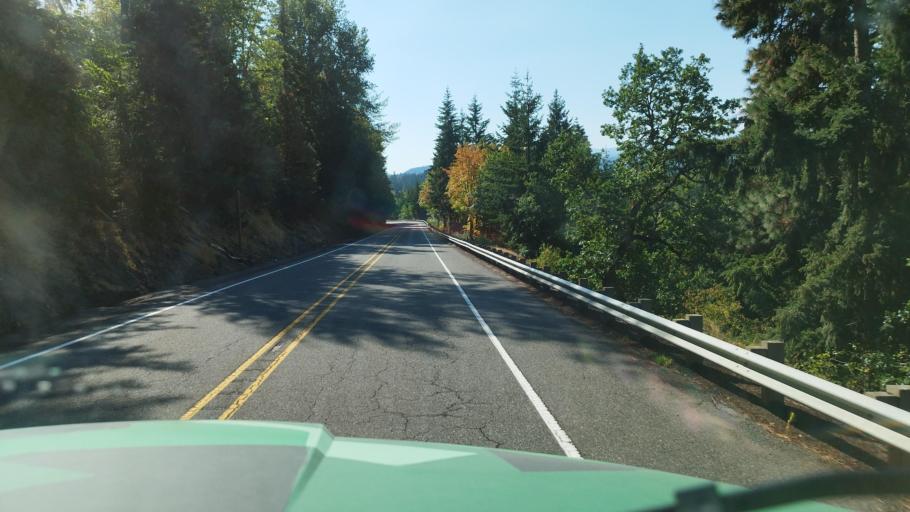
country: US
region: Oregon
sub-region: Hood River County
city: Odell
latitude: 45.5083
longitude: -121.5634
